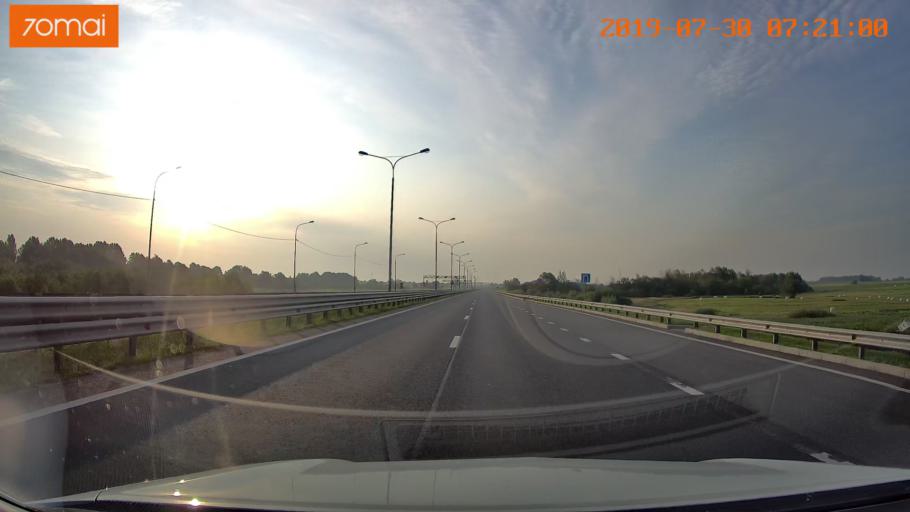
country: RU
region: Kaliningrad
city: Bol'shoe Isakovo
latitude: 54.6984
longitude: 20.7169
